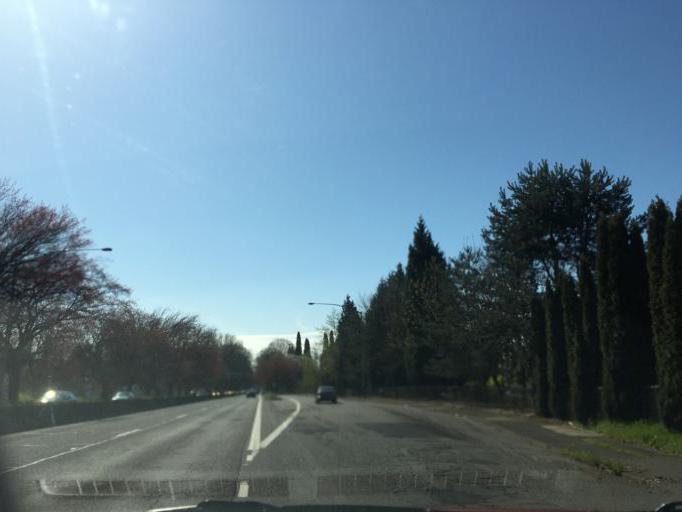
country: US
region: Oregon
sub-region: Clackamas County
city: Milwaukie
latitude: 45.4768
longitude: -122.6411
